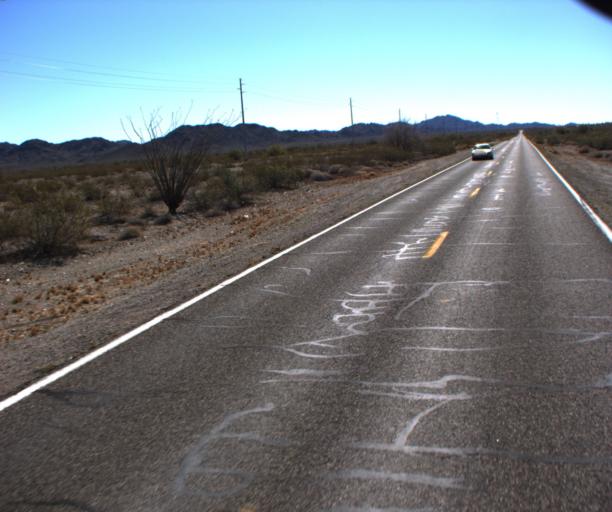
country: US
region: Arizona
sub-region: La Paz County
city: Salome
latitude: 33.7347
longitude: -113.7282
